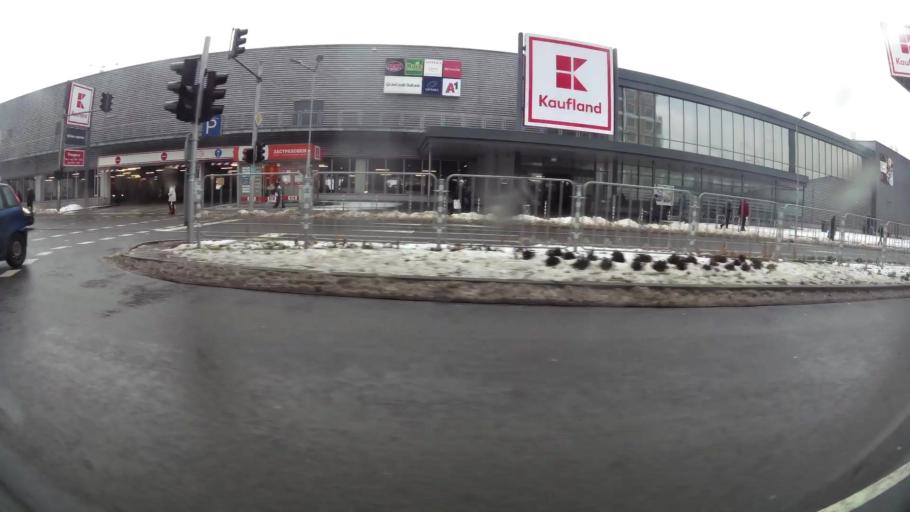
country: BG
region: Sofia-Capital
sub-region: Stolichna Obshtina
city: Sofia
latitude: 42.6708
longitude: 23.2739
